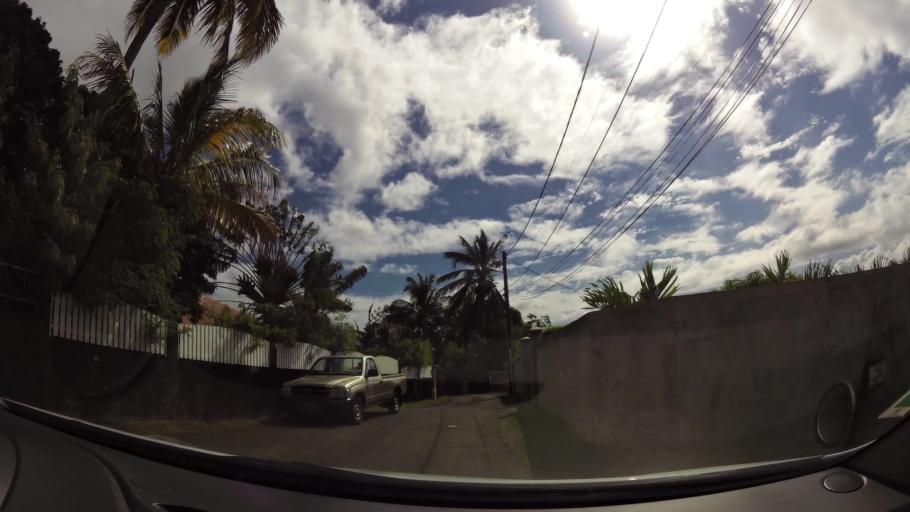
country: RE
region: Reunion
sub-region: Reunion
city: Sainte-Marie
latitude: -20.8988
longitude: 55.5267
